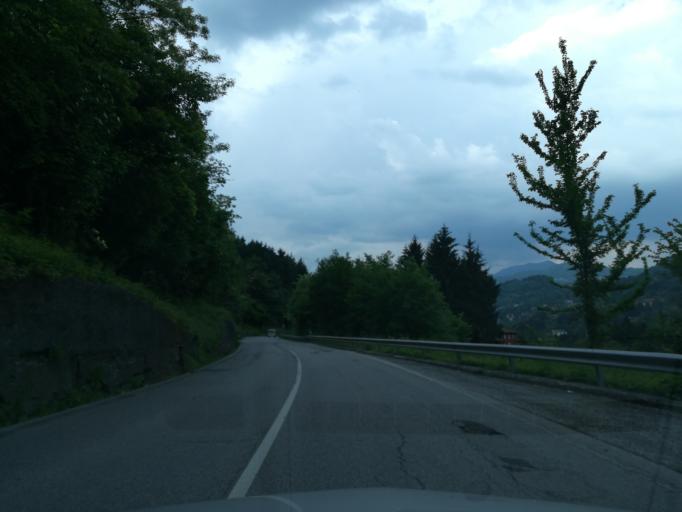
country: IT
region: Lombardy
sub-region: Provincia di Bergamo
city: Strozza
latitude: 45.7787
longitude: 9.5775
